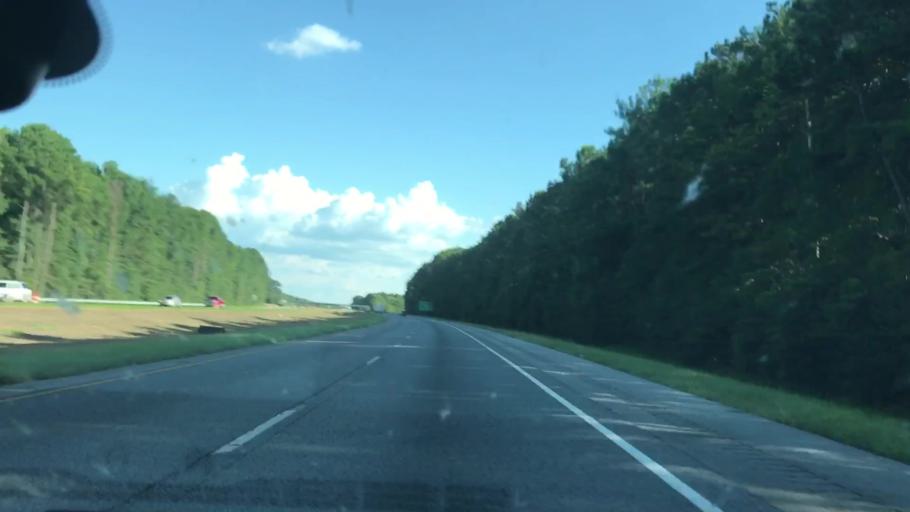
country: US
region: Georgia
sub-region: Harris County
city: Hamilton
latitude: 32.6700
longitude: -84.9867
